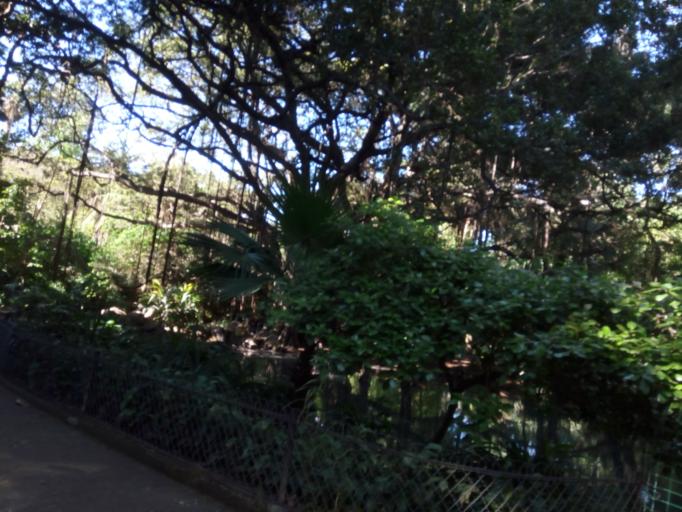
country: DZ
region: Alger
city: Algiers
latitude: 36.7457
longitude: 3.0771
